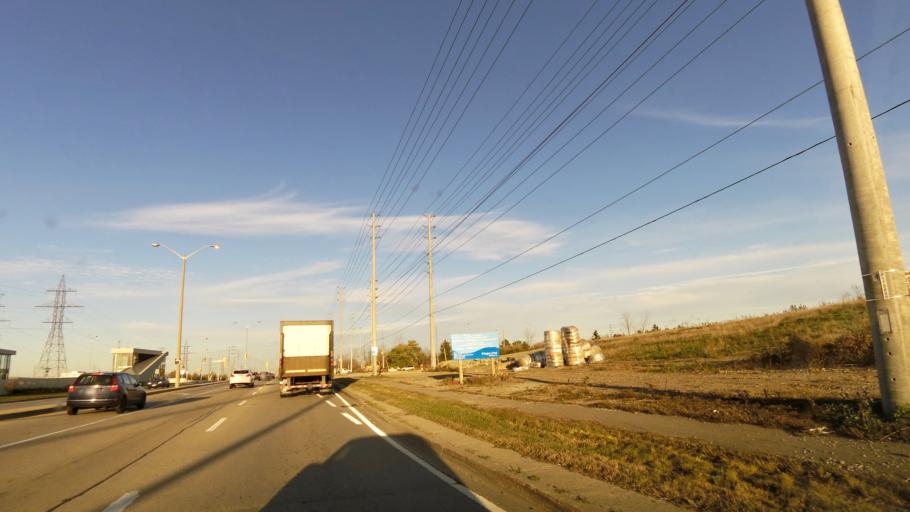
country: CA
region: Ontario
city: Etobicoke
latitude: 43.6293
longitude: -79.6149
